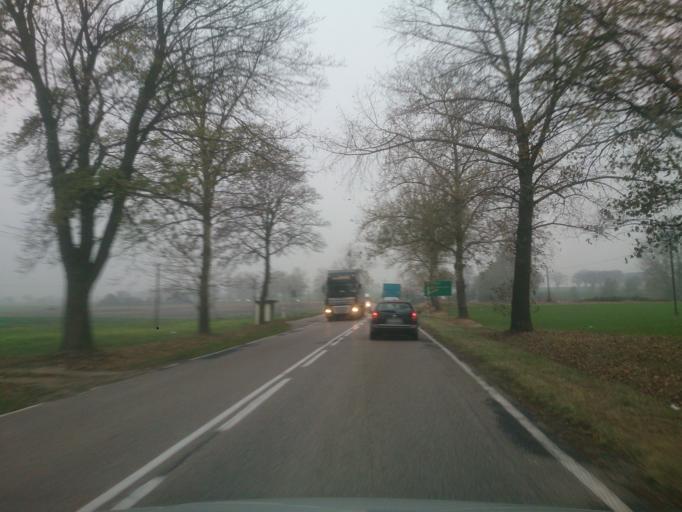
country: PL
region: Kujawsko-Pomorskie
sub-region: Powiat brodnicki
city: Bobrowo
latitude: 53.2267
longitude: 19.2086
